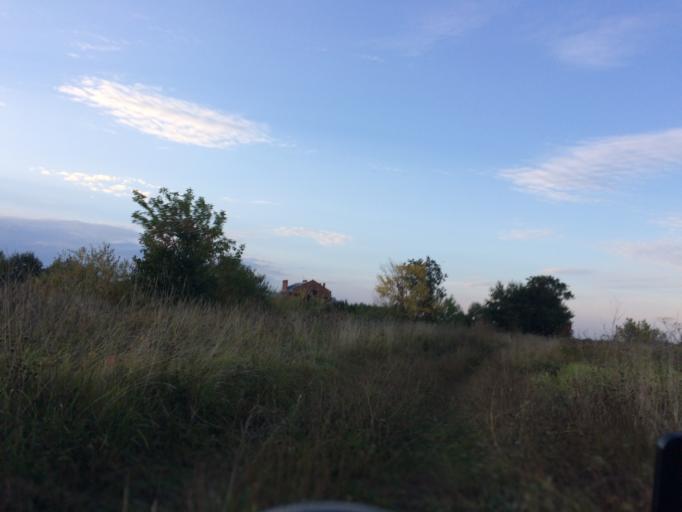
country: RU
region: Mariy-El
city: Yoshkar-Ola
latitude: 56.6493
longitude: 47.9206
